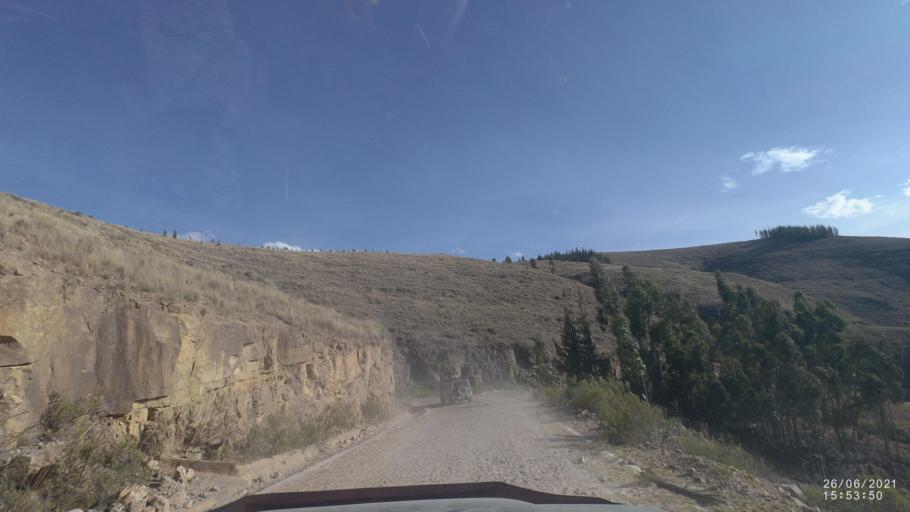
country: BO
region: Cochabamba
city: Arani
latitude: -17.8390
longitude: -65.7075
